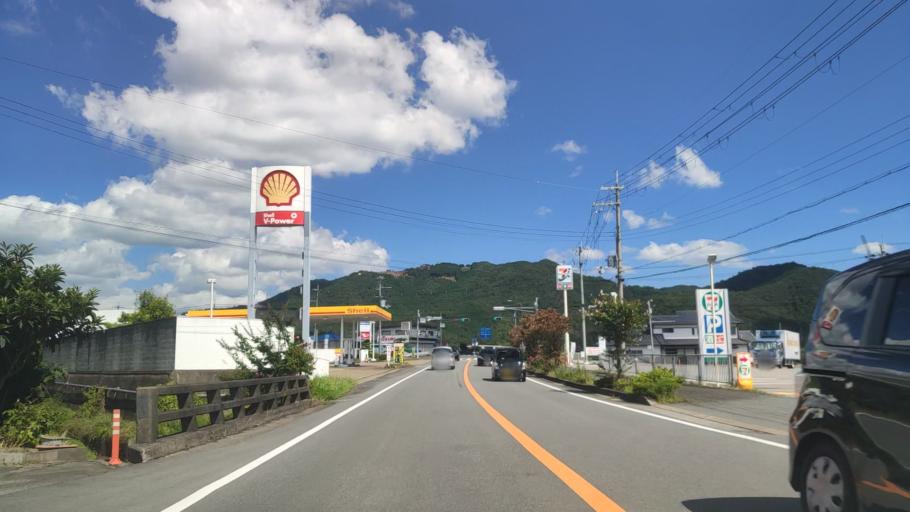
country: JP
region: Kyoto
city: Fukuchiyama
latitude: 35.2066
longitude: 135.1319
